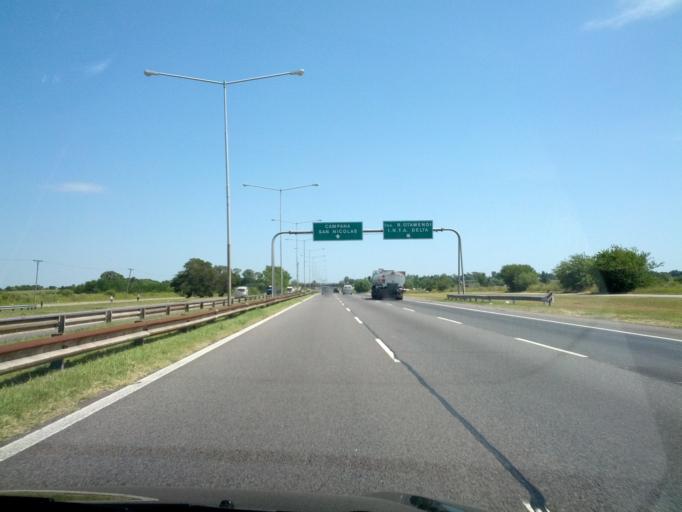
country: AR
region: Buenos Aires
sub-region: Partido de Campana
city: Campana
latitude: -34.2352
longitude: -58.9120
